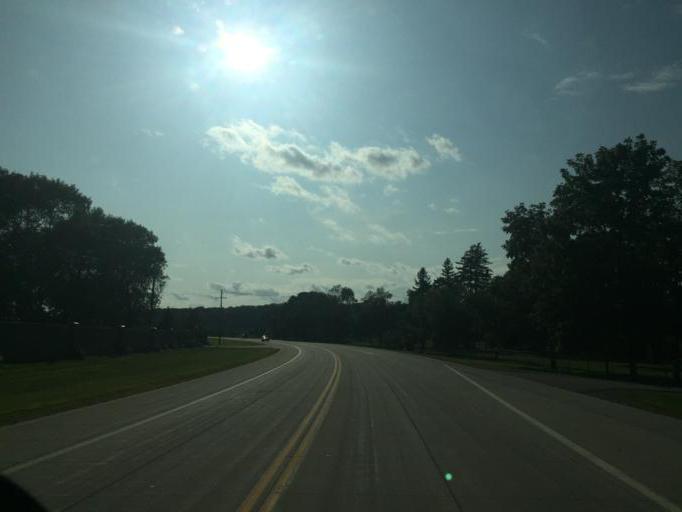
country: US
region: Minnesota
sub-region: Olmsted County
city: Rochester
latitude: 44.0039
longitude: -92.5127
